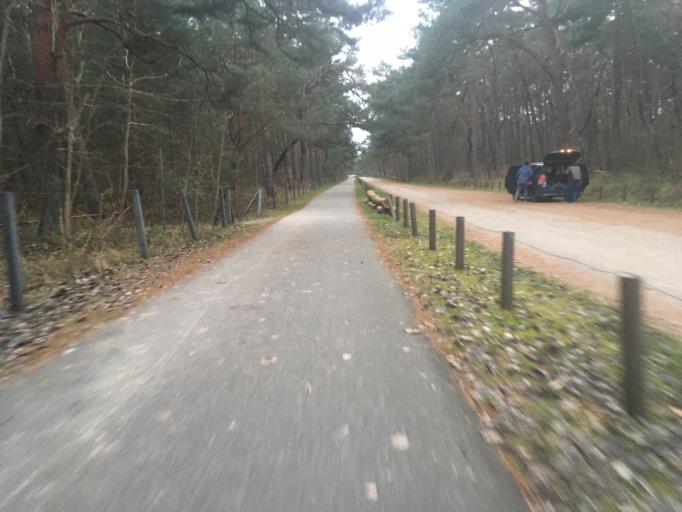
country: DE
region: Mecklenburg-Vorpommern
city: Sagard
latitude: 54.4698
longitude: 13.5681
